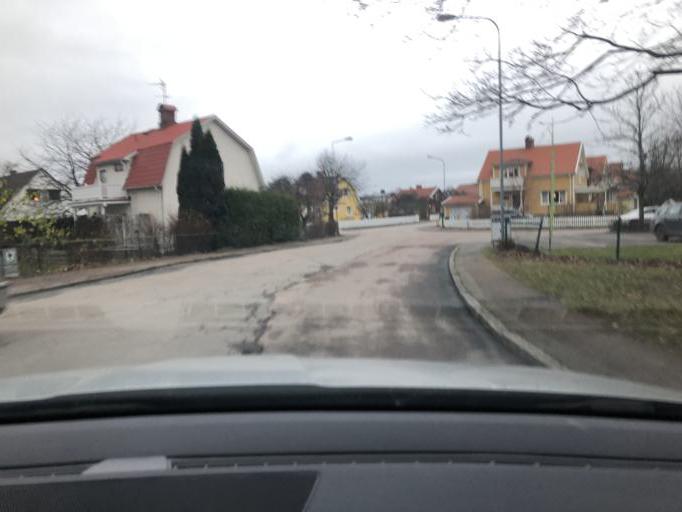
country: SE
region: Vaermland
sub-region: Karlstads Kommun
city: Karlstad
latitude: 59.3937
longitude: 13.5115
